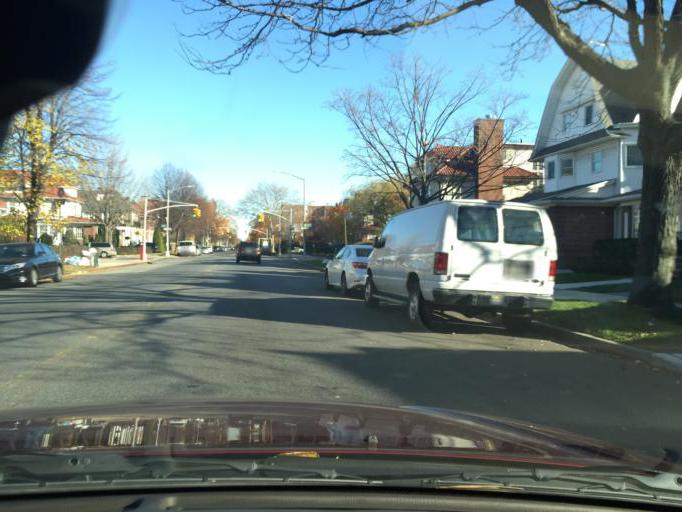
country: US
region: New York
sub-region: Kings County
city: Brooklyn
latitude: 40.6244
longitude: -73.9689
